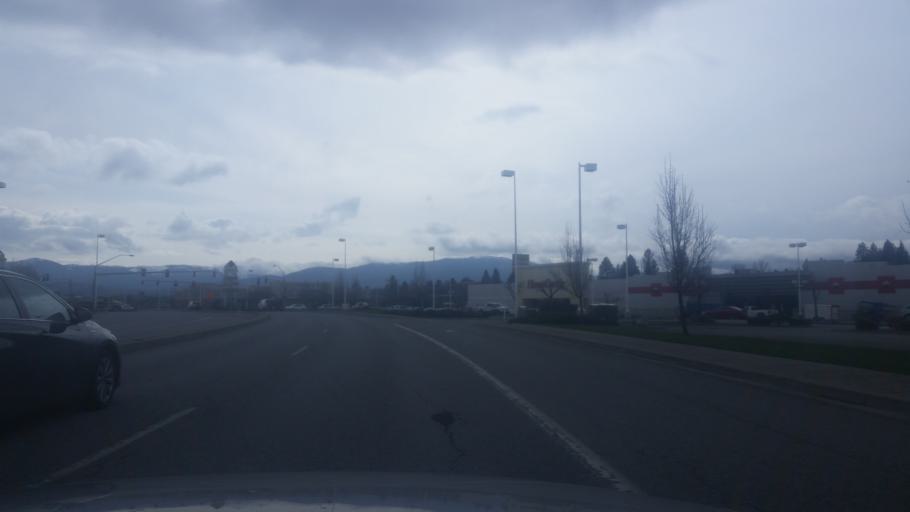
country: US
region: Washington
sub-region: Spokane County
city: Veradale
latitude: 47.6723
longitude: -117.2015
